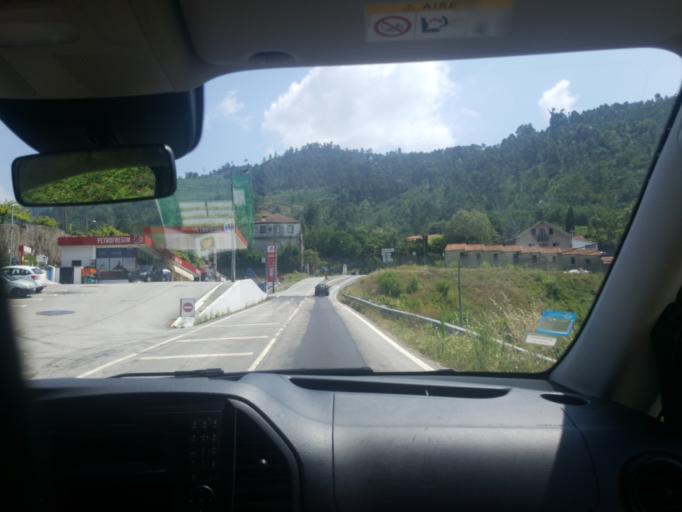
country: PT
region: Porto
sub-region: Amarante
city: Amarante
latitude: 41.2462
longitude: -8.0360
